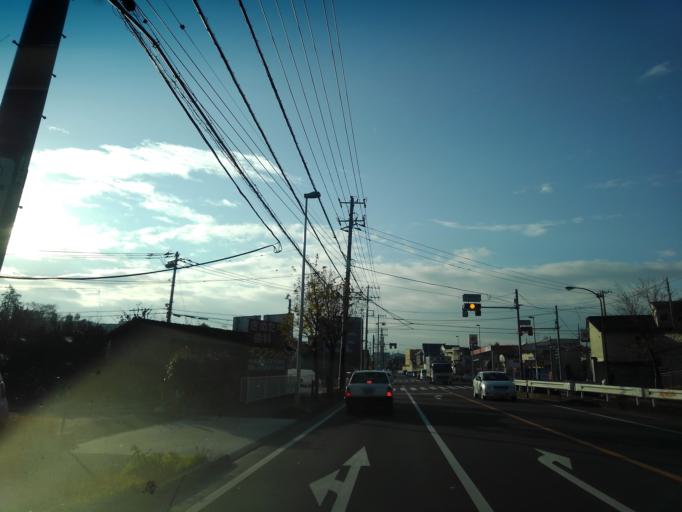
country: JP
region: Tokyo
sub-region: Machida-shi
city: Machida
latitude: 35.5654
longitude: 139.4445
